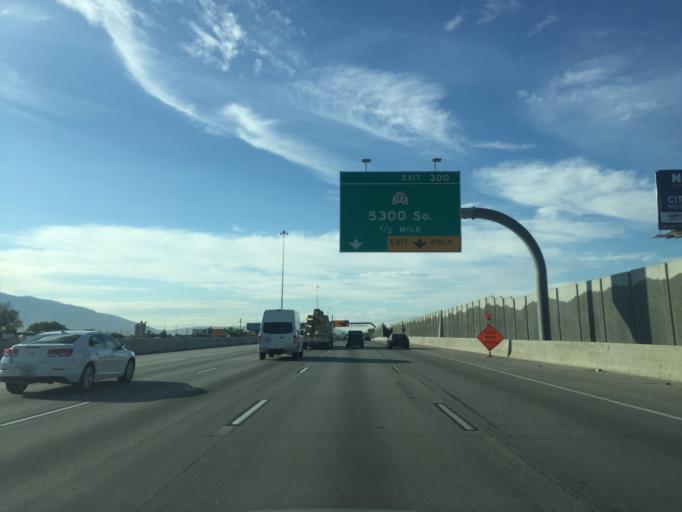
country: US
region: Utah
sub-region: Salt Lake County
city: Murray
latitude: 40.6693
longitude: -111.9017
